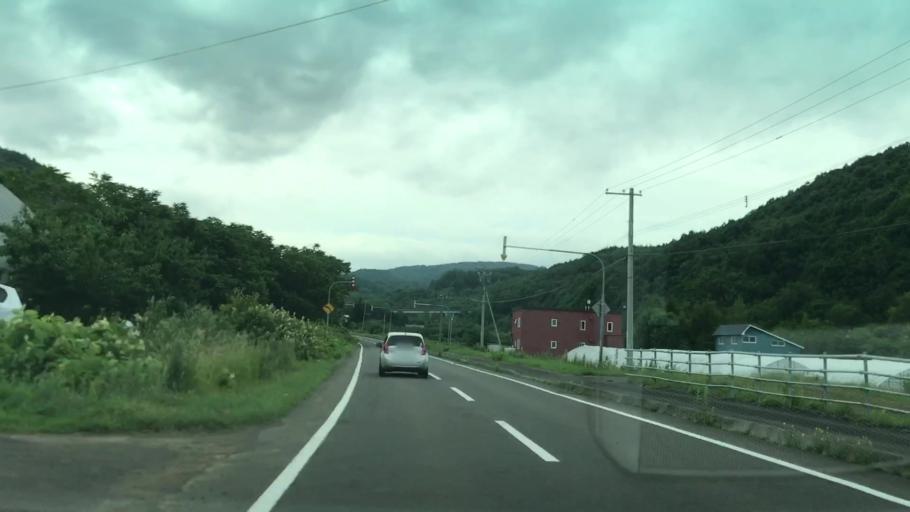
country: JP
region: Hokkaido
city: Yoichi
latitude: 43.1543
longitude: 140.8216
